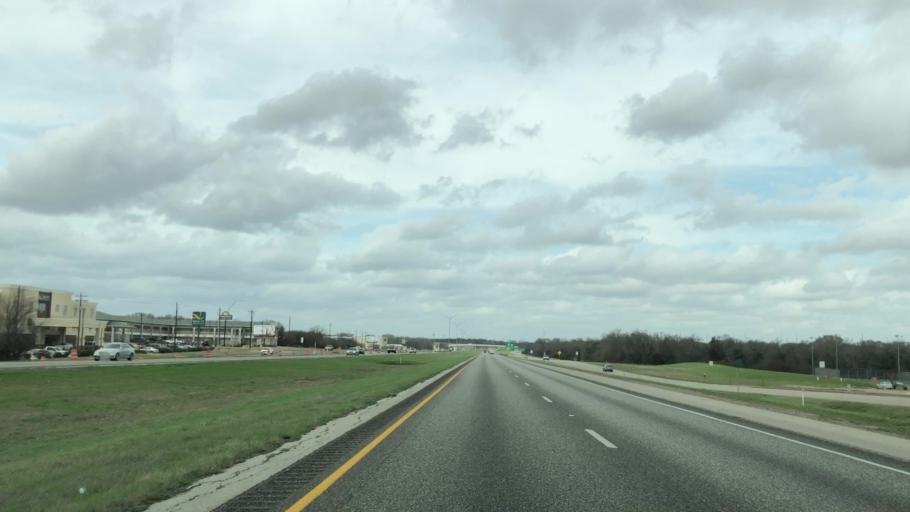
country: US
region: Texas
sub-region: Brazos County
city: Bryan
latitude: 30.6782
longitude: -96.3425
